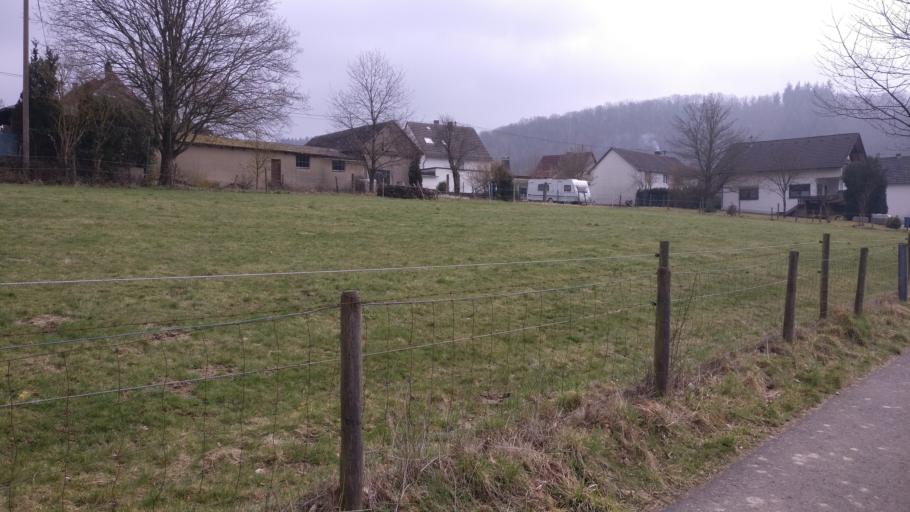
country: DE
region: Rheinland-Pfalz
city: Rossbach
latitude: 50.6199
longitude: 7.4220
